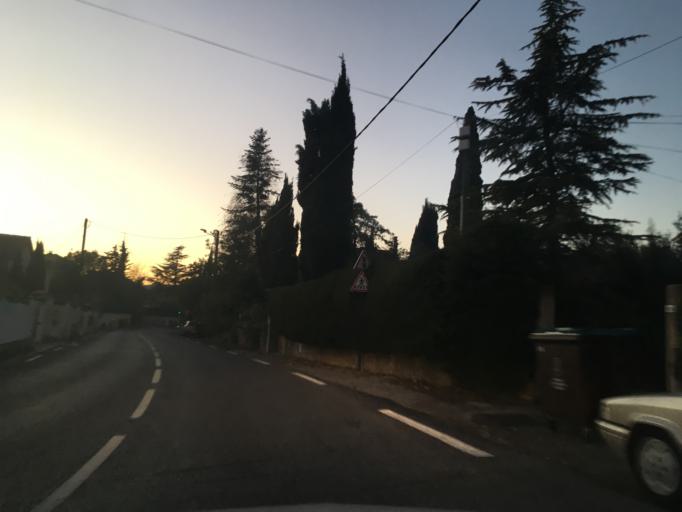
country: FR
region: Provence-Alpes-Cote d'Azur
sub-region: Departement du Var
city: Draguignan
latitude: 43.5387
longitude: 6.4723
